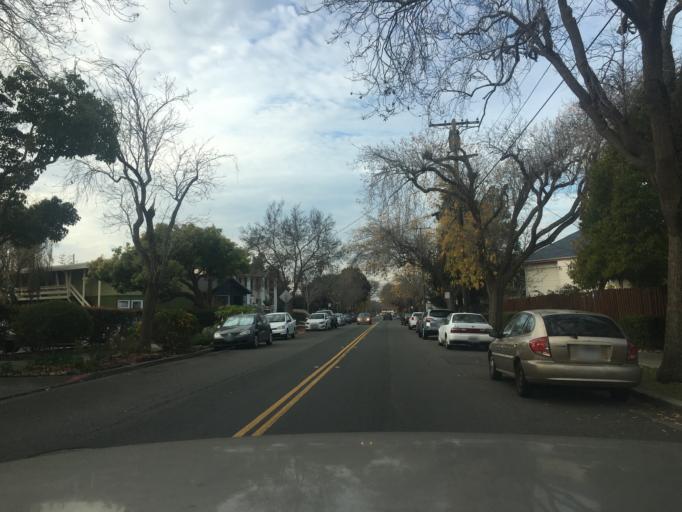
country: US
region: California
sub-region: Alameda County
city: Albany
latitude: 37.8780
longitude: -122.2890
